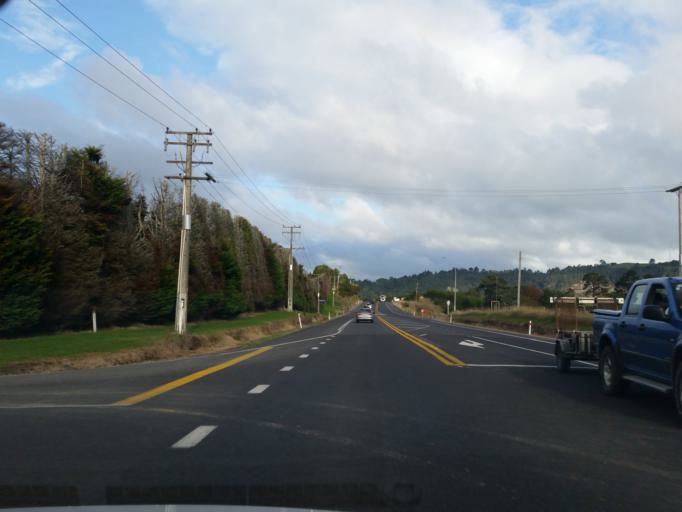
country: NZ
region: Bay of Plenty
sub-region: Tauranga City
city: Tauranga
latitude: -37.6867
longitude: 176.0386
